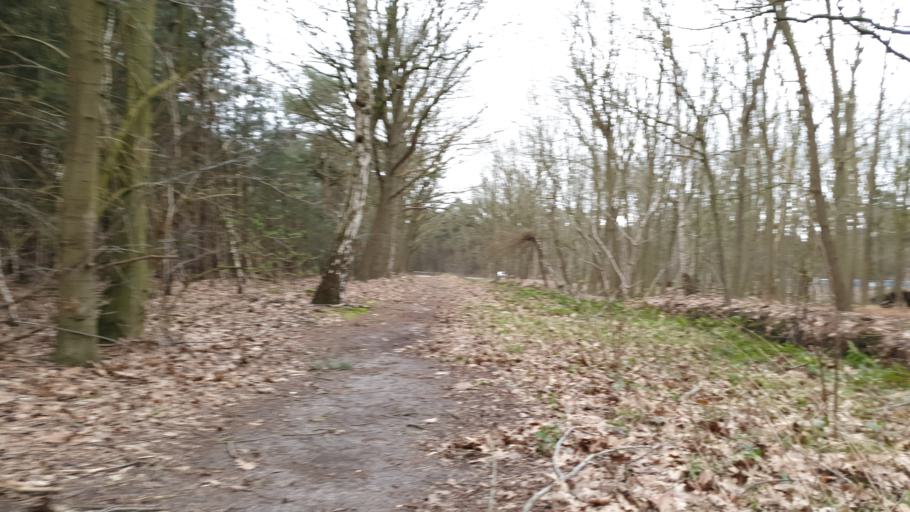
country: NL
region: North Brabant
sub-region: Gemeente Son en Breugel
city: Son
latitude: 51.5075
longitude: 5.4506
